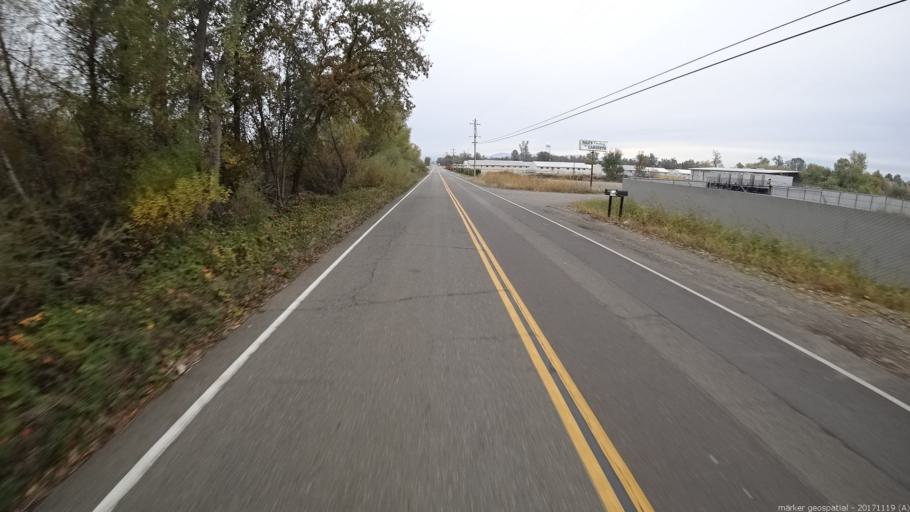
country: US
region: California
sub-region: Shasta County
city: Anderson
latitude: 40.4847
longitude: -122.3506
